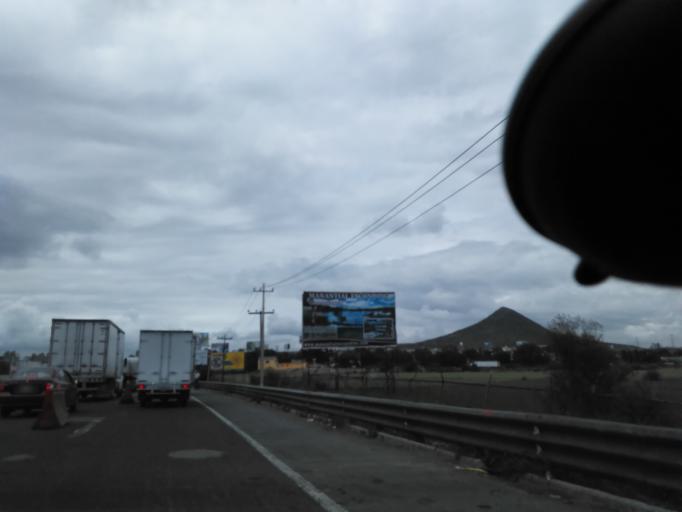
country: MX
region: Mexico
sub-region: Huehuetoca
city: Jorobas
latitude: 19.8210
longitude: -99.2443
